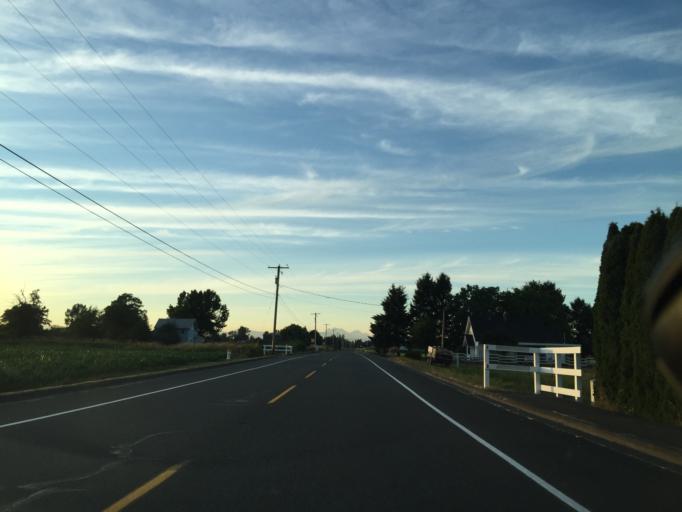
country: US
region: Washington
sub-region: Whatcom County
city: Everson
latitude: 48.9244
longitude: -122.3425
